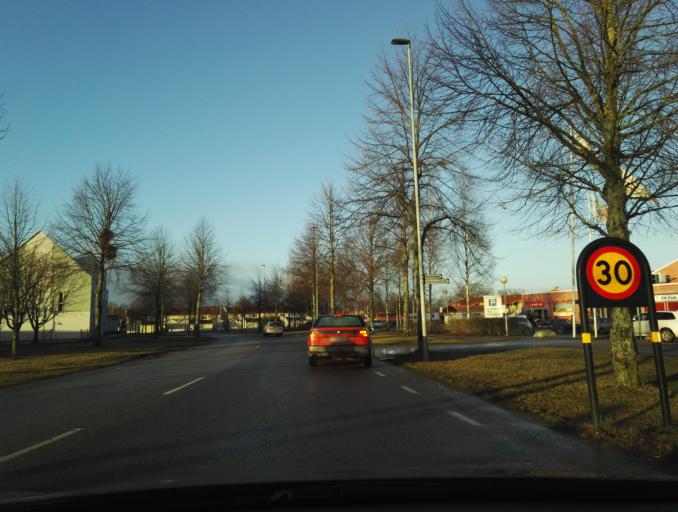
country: SE
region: Kronoberg
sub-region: Vaxjo Kommun
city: Vaexjoe
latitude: 56.9087
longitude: 14.7982
